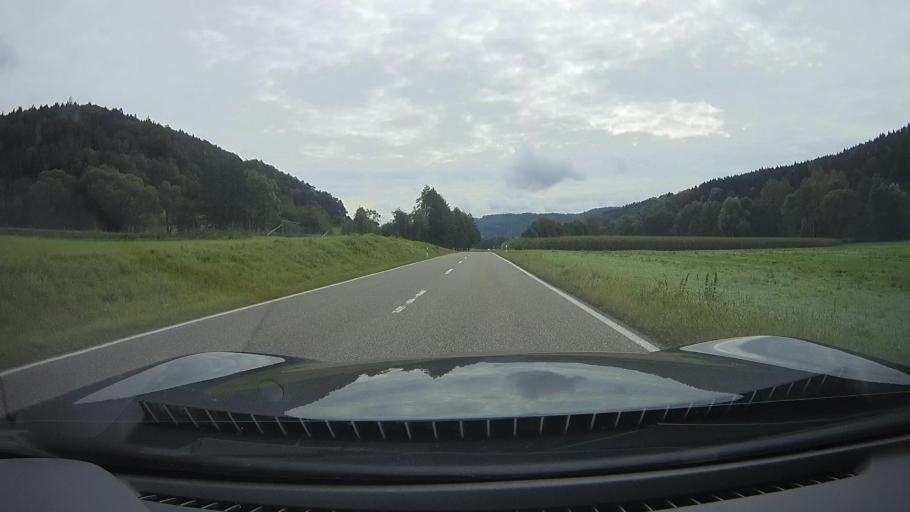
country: DE
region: Baden-Wuerttemberg
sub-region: Regierungsbezirk Stuttgart
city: Sulzbach an der Murr
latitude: 49.0155
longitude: 9.4716
